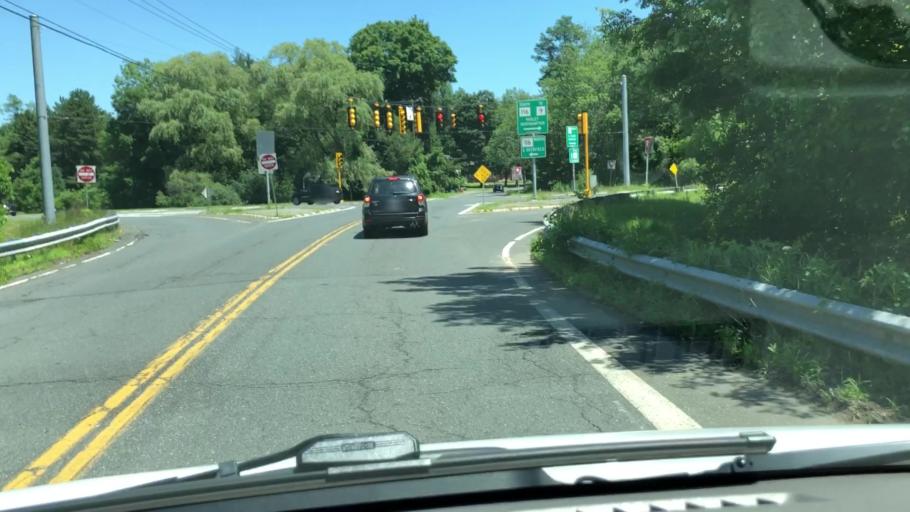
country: US
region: Massachusetts
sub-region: Hampshire County
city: North Amherst
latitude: 42.4087
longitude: -72.5385
